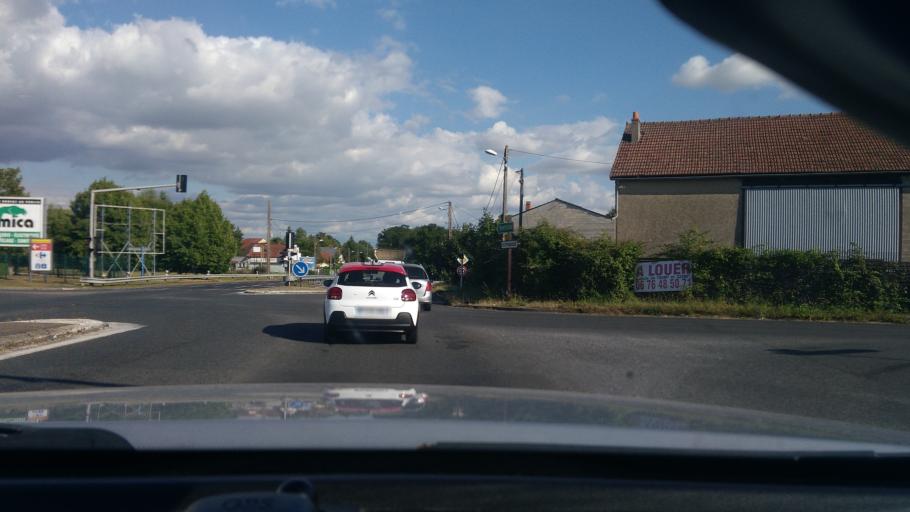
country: FR
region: Ile-de-France
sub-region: Departement de Seine-et-Marne
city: Montereau-Fault-Yonne
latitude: 48.3980
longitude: 2.9416
